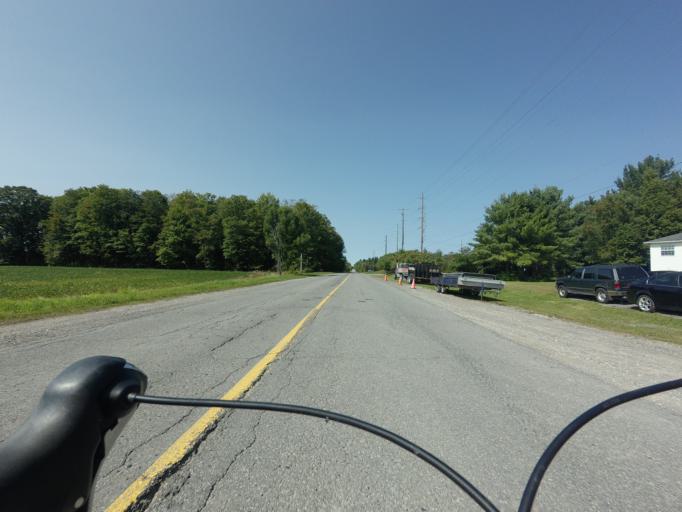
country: CA
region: Ontario
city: Arnprior
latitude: 45.4911
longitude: -76.1374
